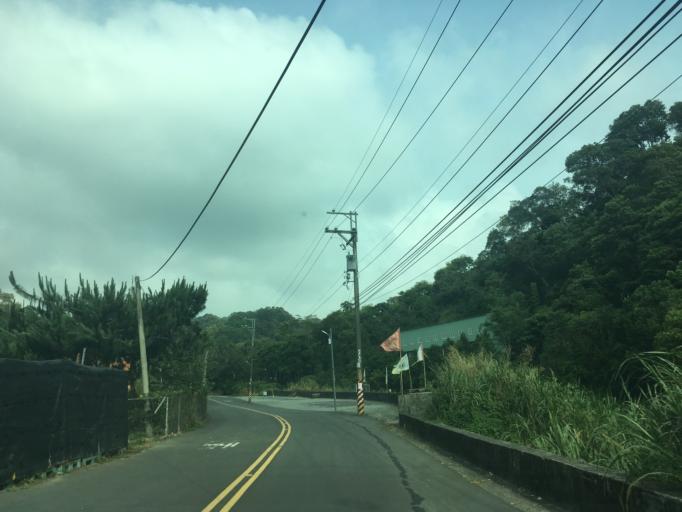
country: TW
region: Taiwan
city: Fengyuan
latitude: 24.2269
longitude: 120.7531
